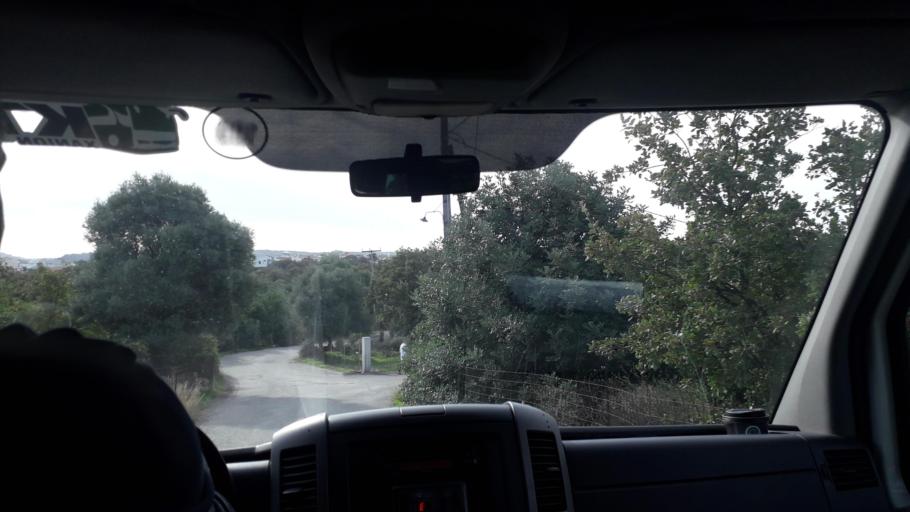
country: GR
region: Crete
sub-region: Nomos Rethymnis
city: Atsipopoulon
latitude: 35.3600
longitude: 24.4321
